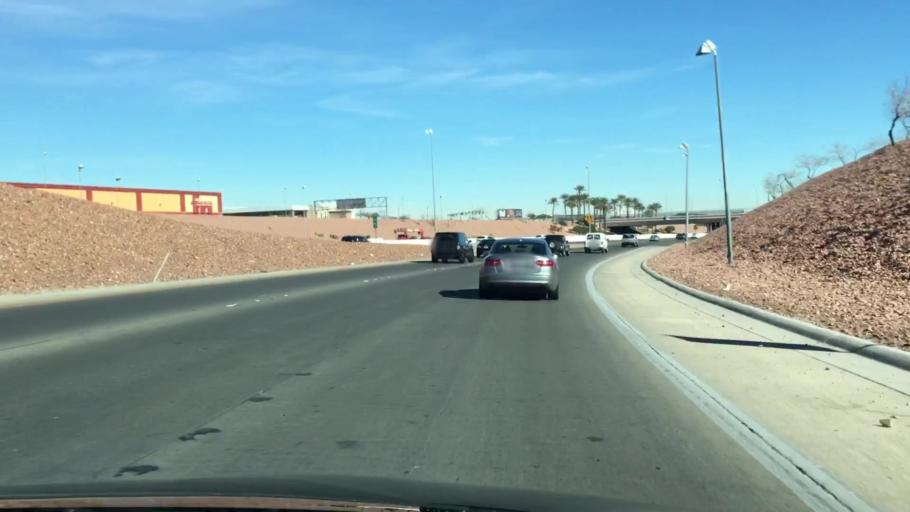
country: US
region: Nevada
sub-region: Clark County
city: Paradise
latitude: 36.0629
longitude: -115.1762
